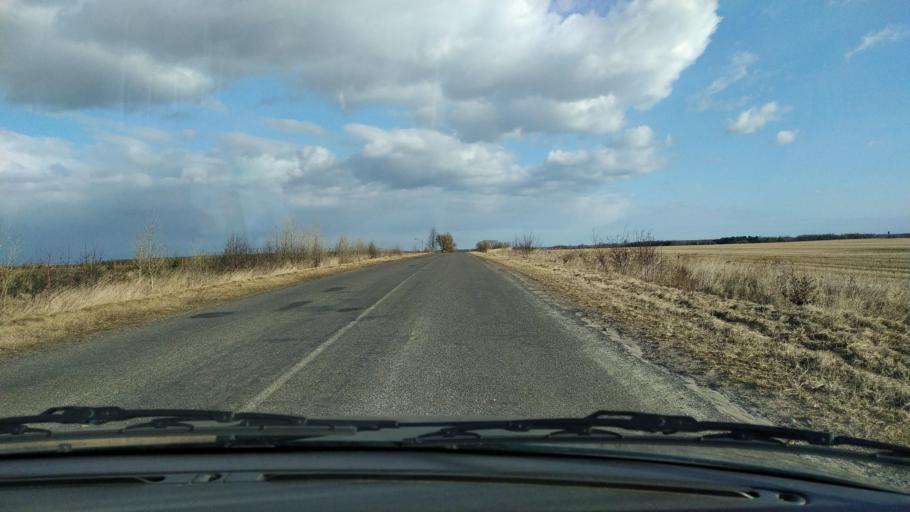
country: BY
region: Brest
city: Kamyanyets
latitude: 52.4177
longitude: 23.8046
